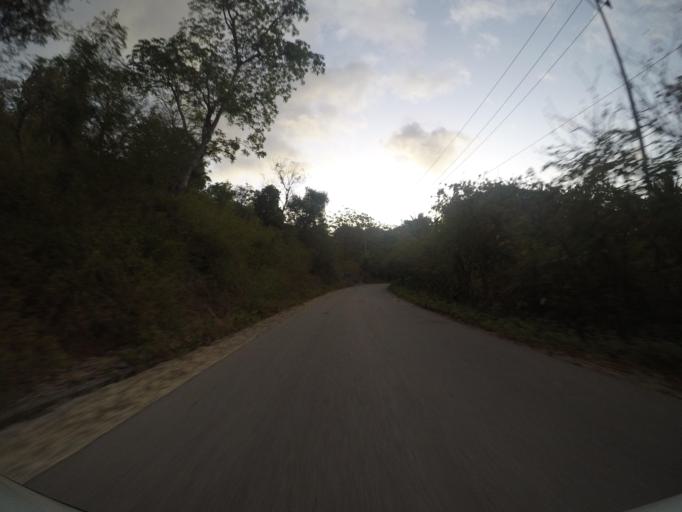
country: TL
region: Lautem
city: Lospalos
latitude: -8.3654
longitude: 127.0503
